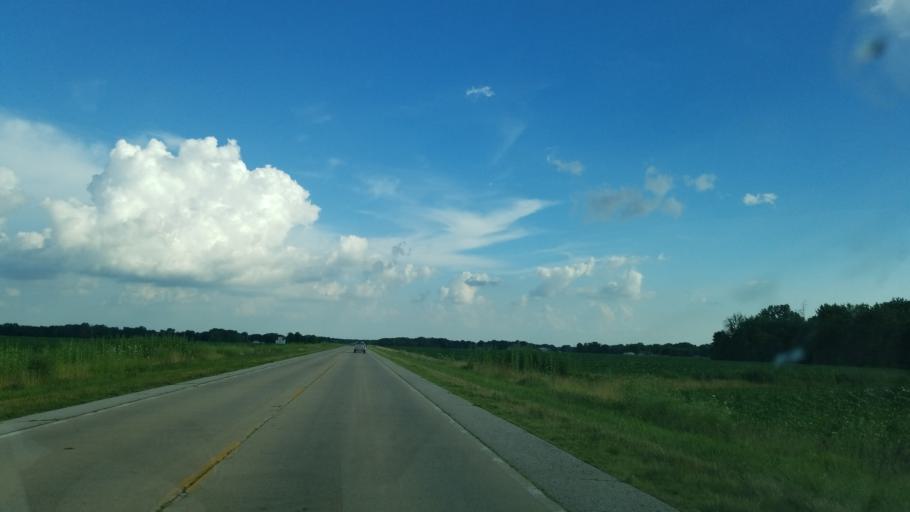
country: US
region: Illinois
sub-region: Marion County
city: Sandoval
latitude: 38.5976
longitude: -89.1084
